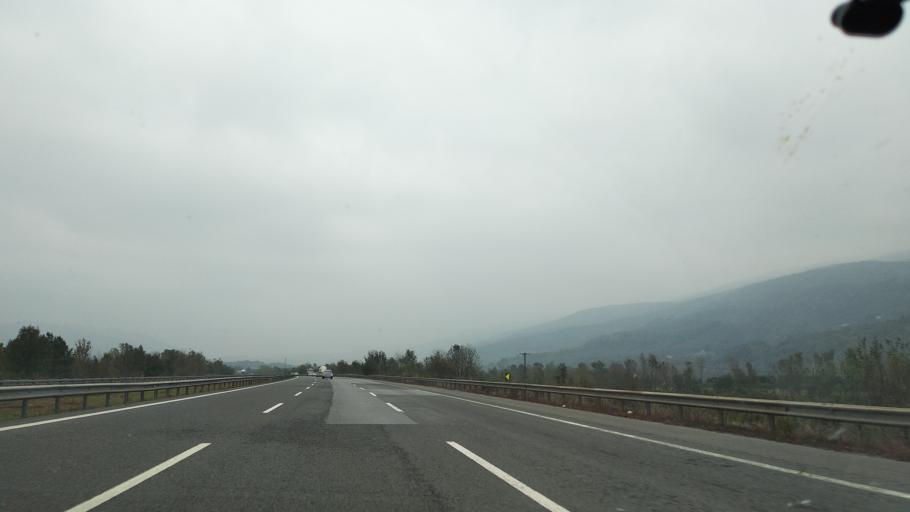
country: TR
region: Sakarya
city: Karadere
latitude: 40.7870
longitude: 30.8240
